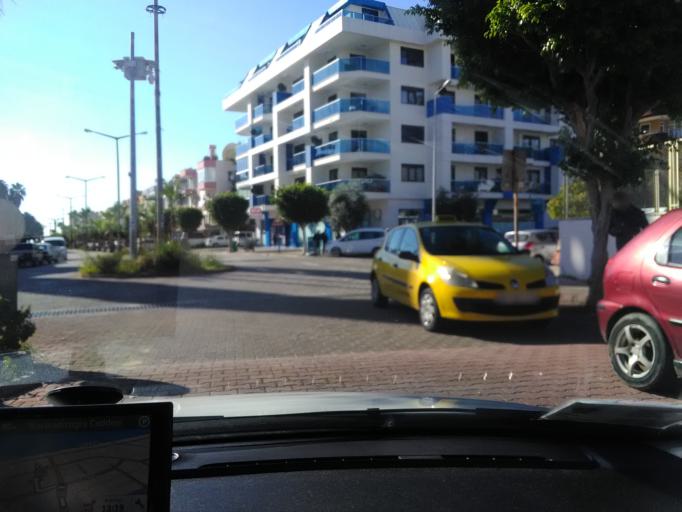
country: TR
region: Antalya
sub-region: Alanya
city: Alanya
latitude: 36.5350
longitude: 32.0421
